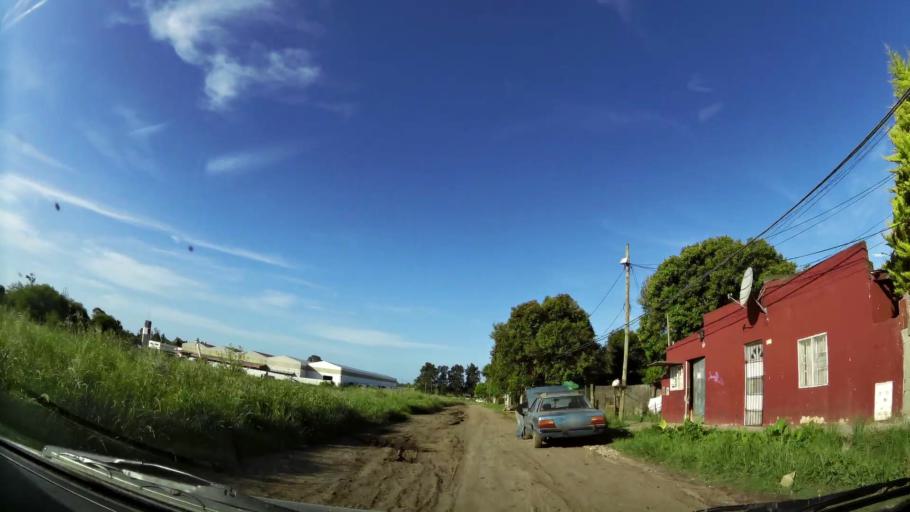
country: AR
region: Buenos Aires
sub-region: Partido de Quilmes
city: Quilmes
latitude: -34.8246
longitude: -58.2206
